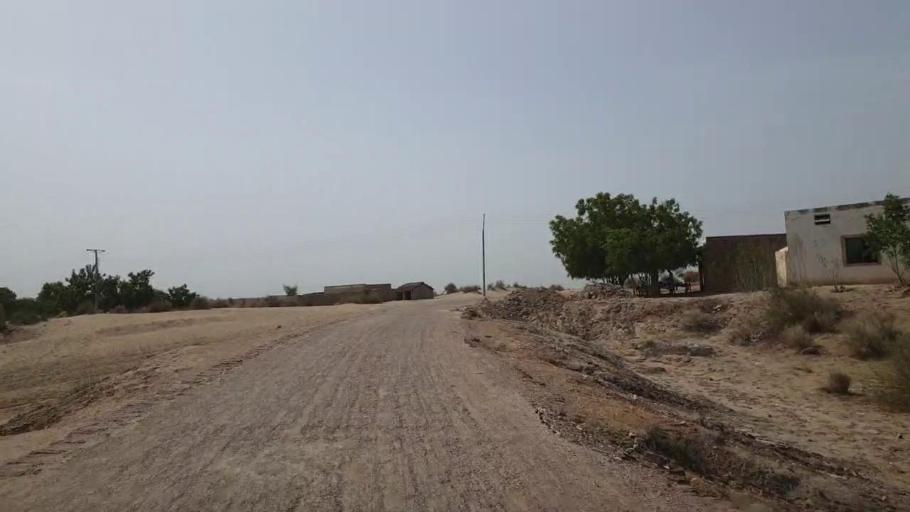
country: PK
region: Sindh
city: Bandhi
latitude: 26.5388
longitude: 68.3871
